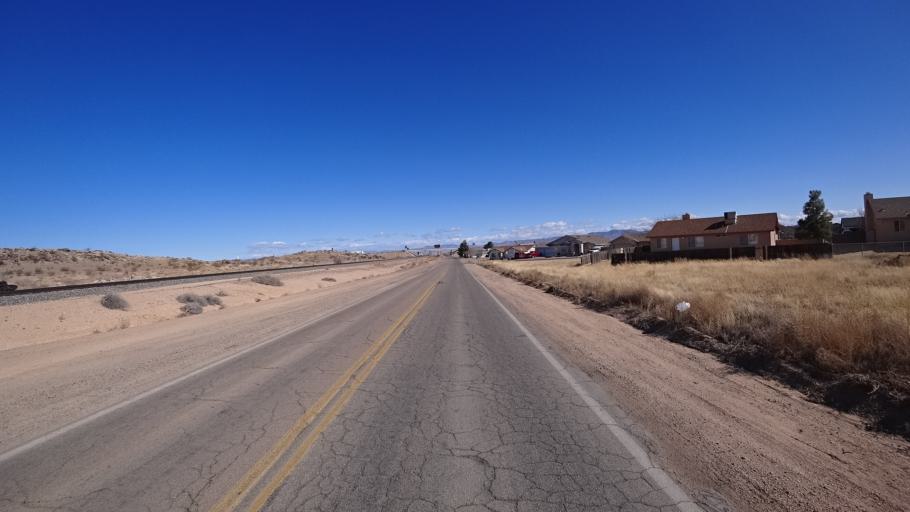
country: US
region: Arizona
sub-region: Mohave County
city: Kingman
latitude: 35.2130
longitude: -114.0109
